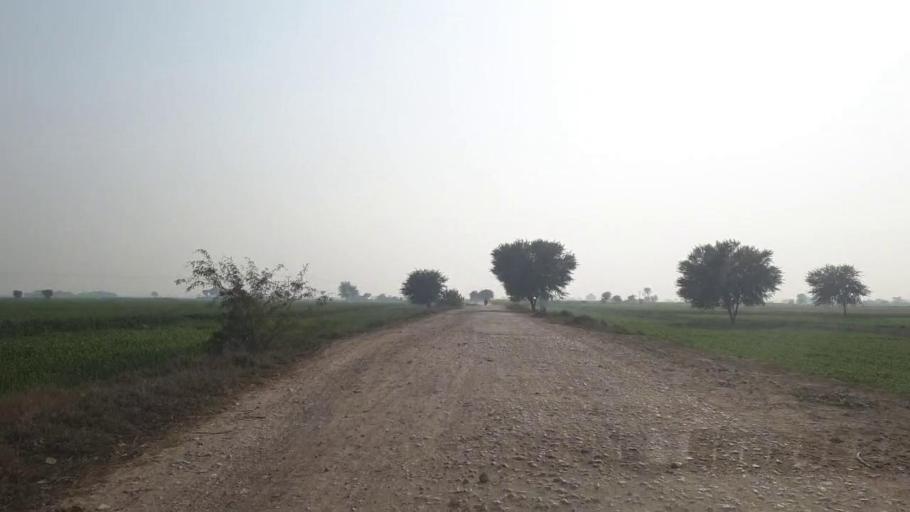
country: PK
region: Sindh
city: Hala
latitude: 25.7609
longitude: 68.3844
